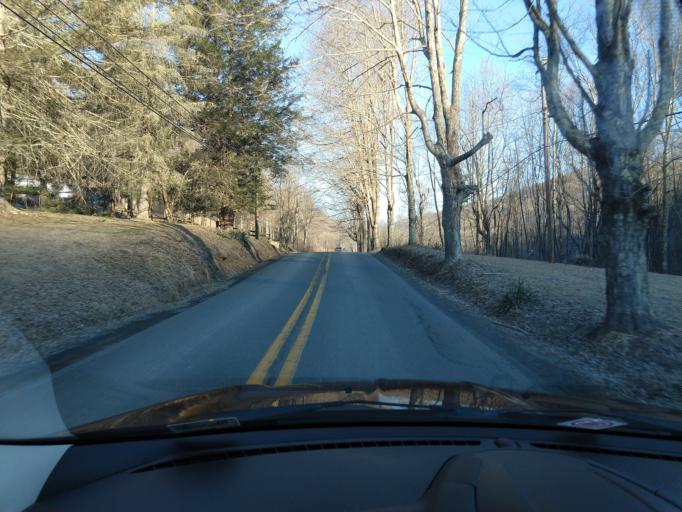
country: US
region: West Virginia
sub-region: Greenbrier County
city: Rainelle
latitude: 37.9487
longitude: -80.7362
